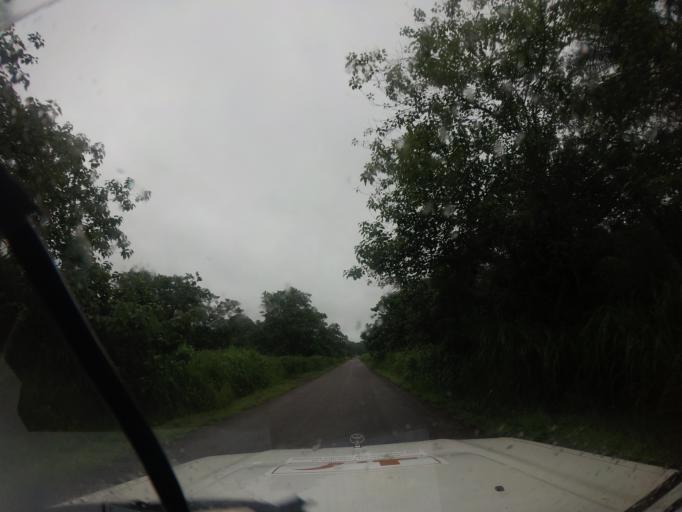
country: SL
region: Northern Province
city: Kabala
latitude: 9.4832
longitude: -11.6241
